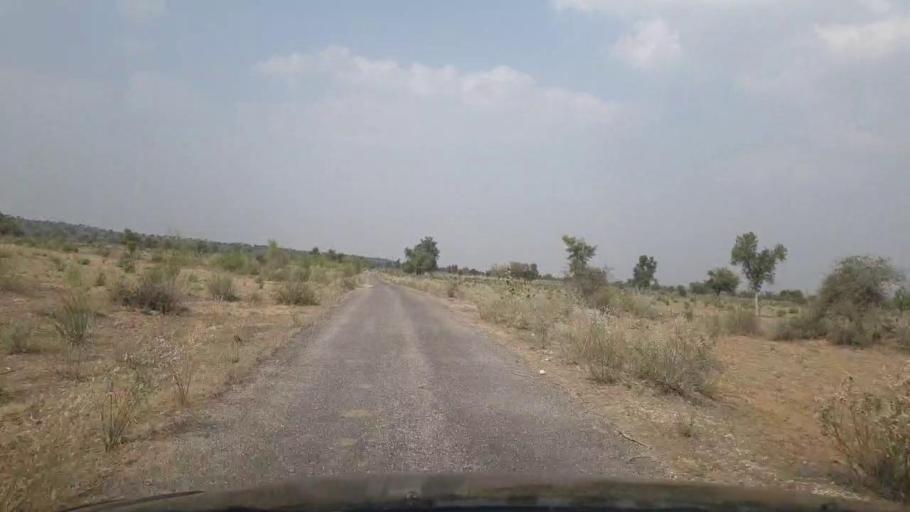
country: PK
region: Sindh
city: Islamkot
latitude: 24.9038
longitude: 70.5583
